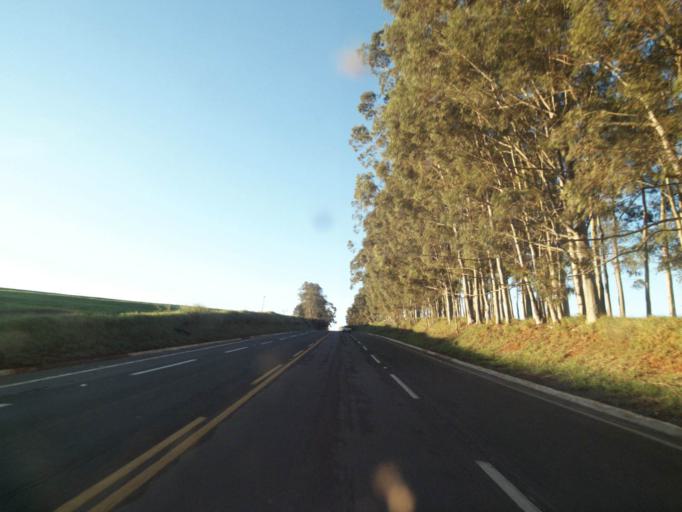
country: BR
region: Parana
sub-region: Faxinal
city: Faxinal
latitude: -23.7339
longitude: -51.1263
